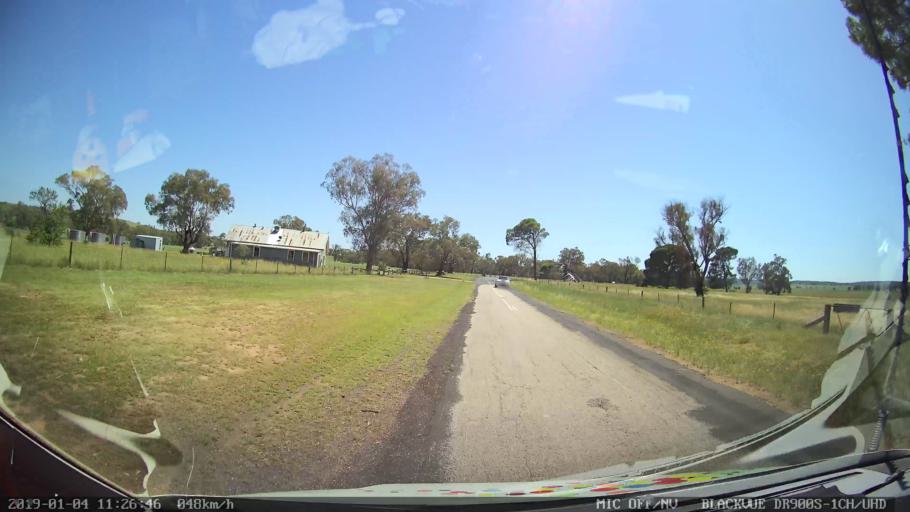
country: AU
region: New South Wales
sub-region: Cabonne
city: Molong
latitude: -33.1130
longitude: 148.7572
